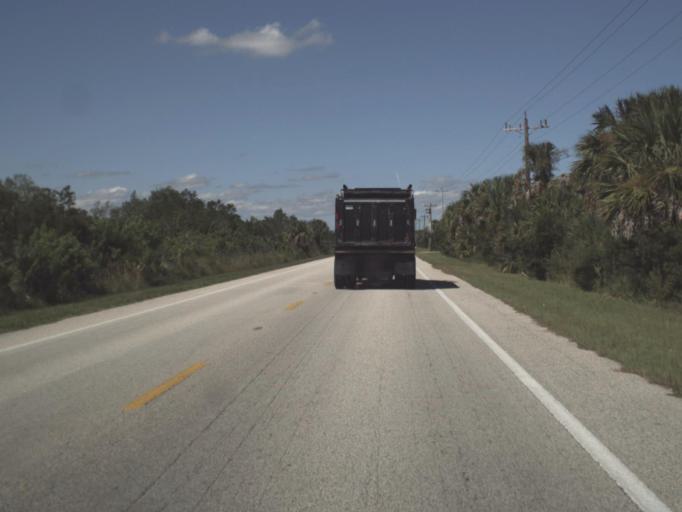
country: US
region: Florida
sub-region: Collier County
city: Marco
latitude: 25.9396
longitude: -81.4647
